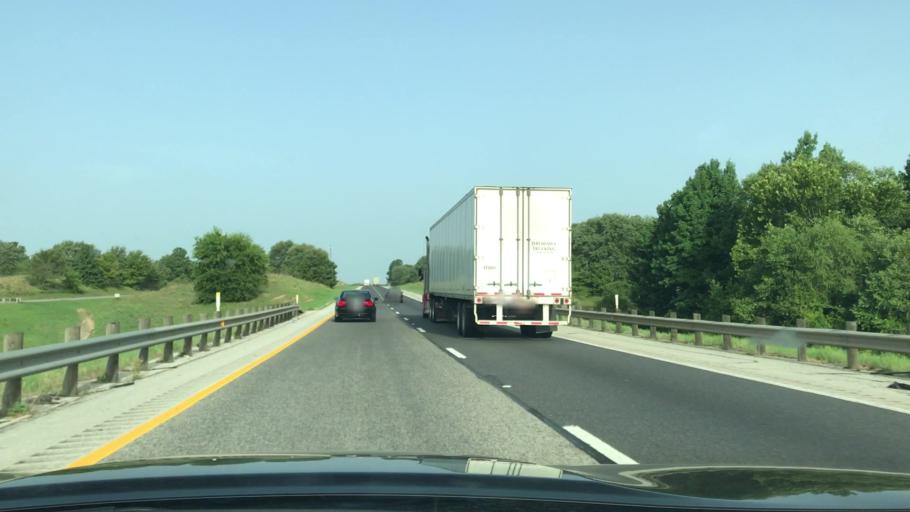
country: US
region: Texas
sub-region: Smith County
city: Tyler
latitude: 32.4525
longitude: -95.2648
